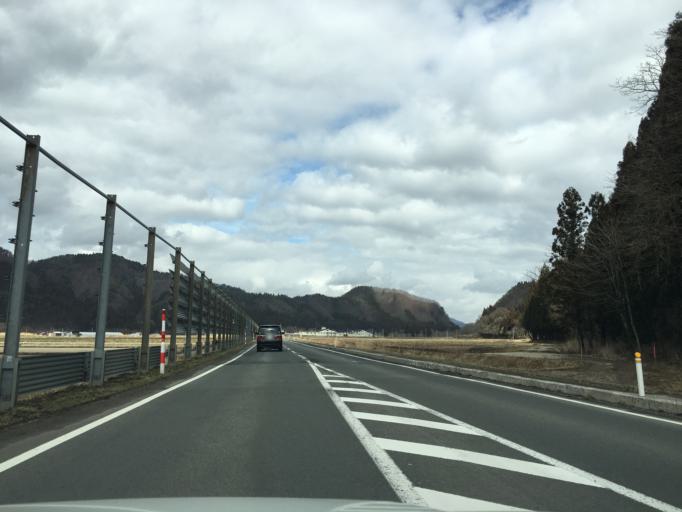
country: JP
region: Akita
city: Hanawa
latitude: 40.2368
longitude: 140.7364
